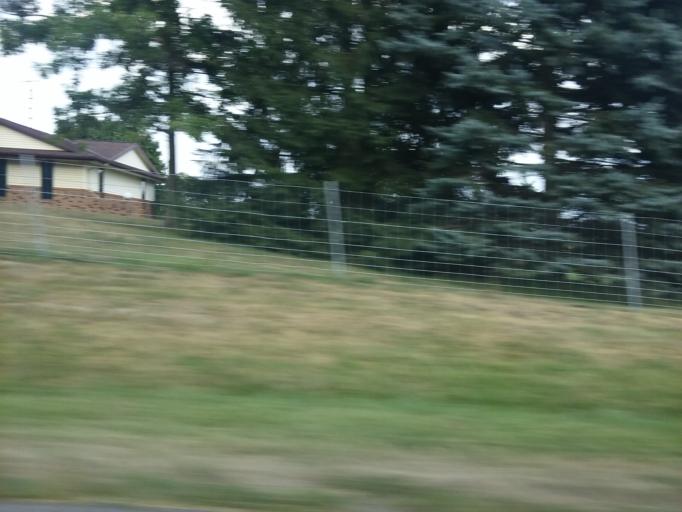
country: US
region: Ohio
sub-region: Wood County
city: Bowling Green
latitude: 41.2874
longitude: -83.6502
